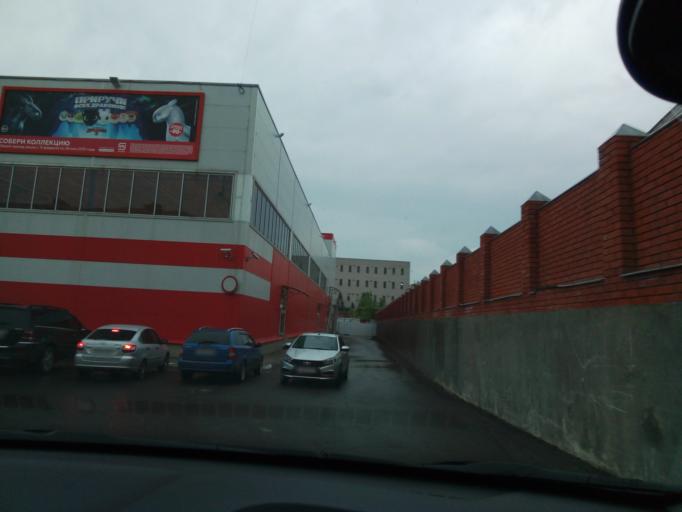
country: RU
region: Chuvashia
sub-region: Cheboksarskiy Rayon
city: Cheboksary
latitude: 56.1232
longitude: 47.2575
